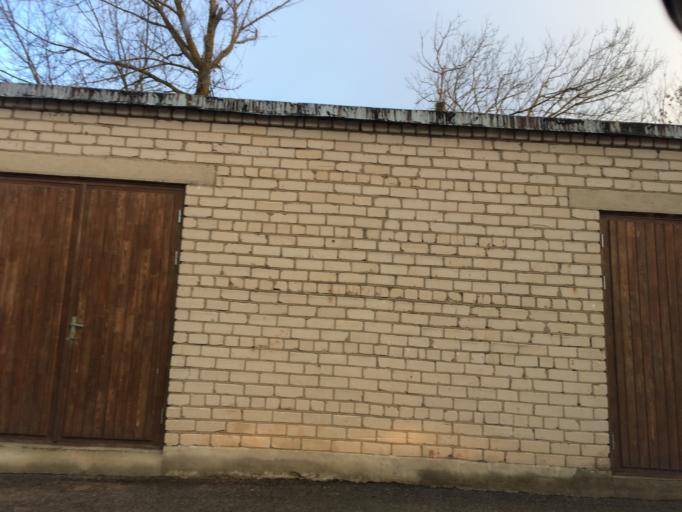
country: LV
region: Rezekne
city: Rezekne
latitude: 56.4967
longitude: 27.3262
